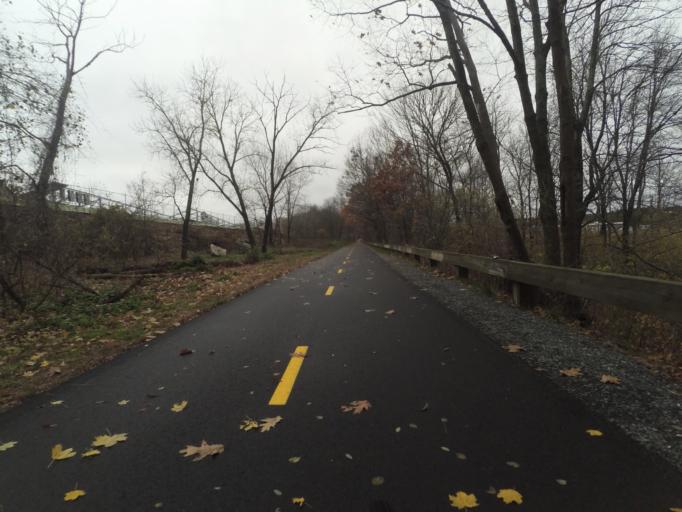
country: US
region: Massachusetts
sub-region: Middlesex County
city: Bedford
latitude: 42.4691
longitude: -71.2529
